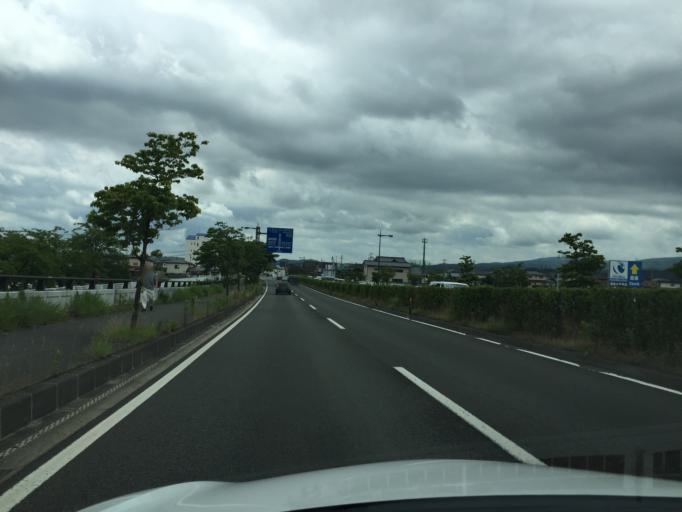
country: JP
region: Fukushima
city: Fukushima-shi
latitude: 37.7523
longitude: 140.4357
